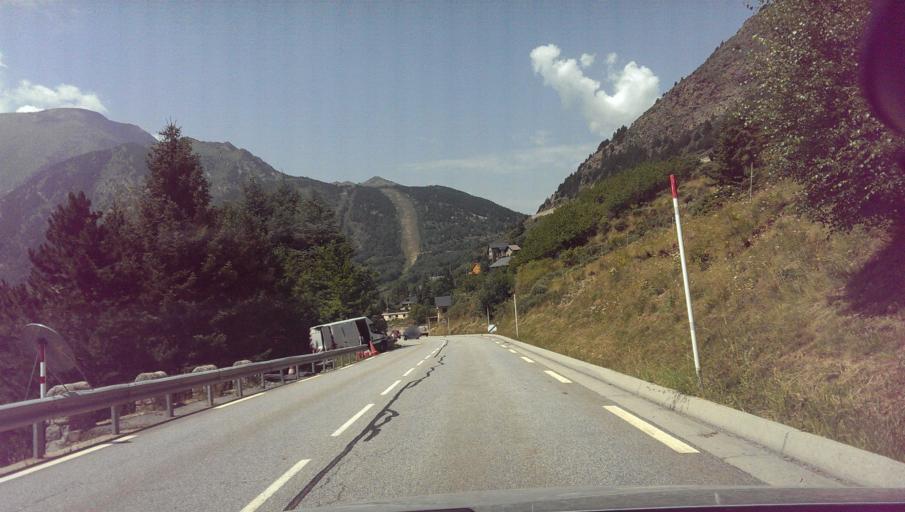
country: AD
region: Encamp
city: Pas de la Casa
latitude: 42.5497
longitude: 1.8355
